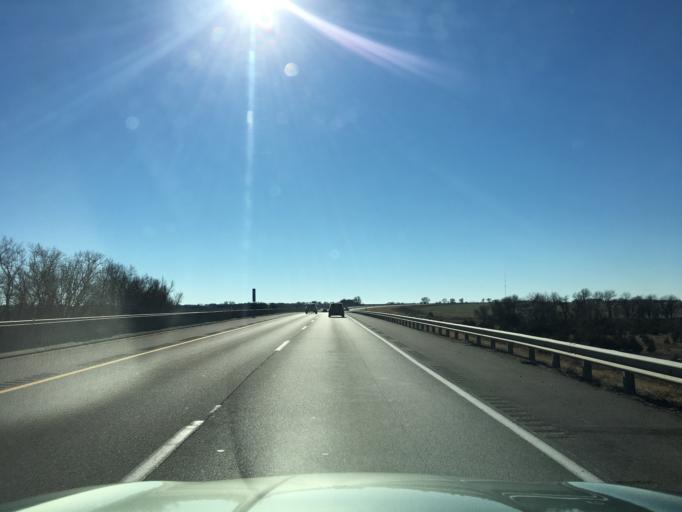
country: US
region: Kansas
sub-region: Sumner County
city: Belle Plaine
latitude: 37.3513
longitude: -97.3221
